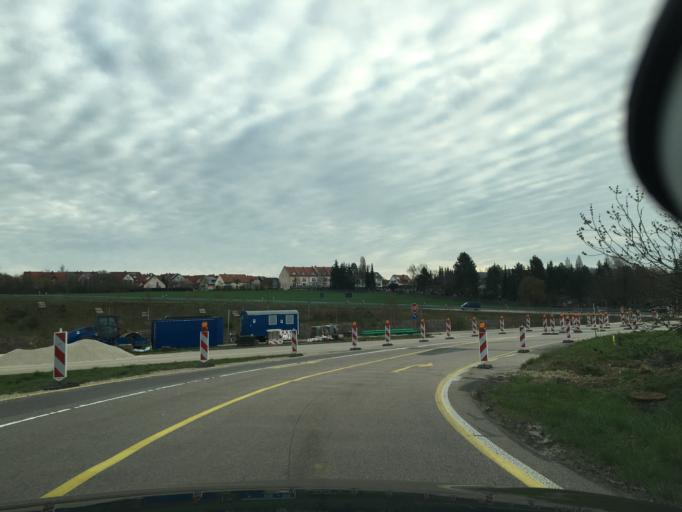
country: DE
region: Bavaria
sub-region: Upper Palatinate
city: Amberg
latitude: 49.4457
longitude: 11.8342
